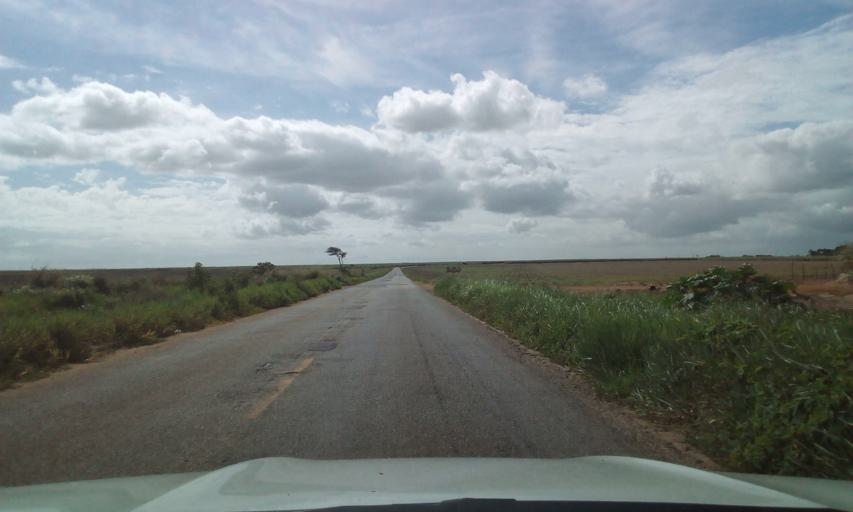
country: BR
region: Paraiba
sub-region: Santa Rita
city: Santa Rita
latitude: -7.0757
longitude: -34.9862
